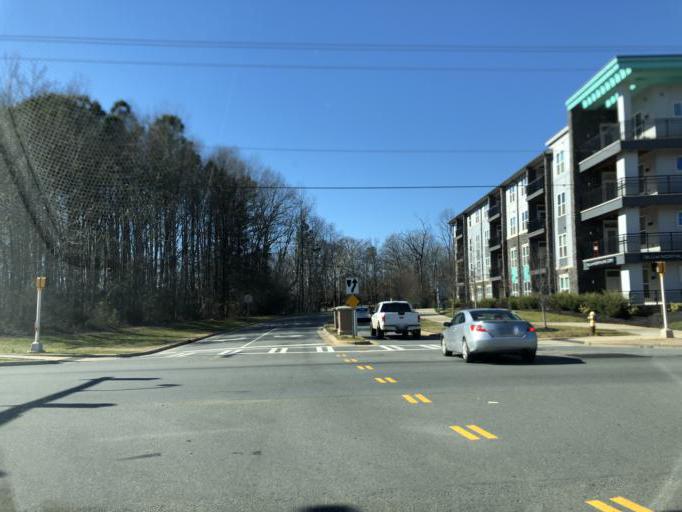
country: US
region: North Carolina
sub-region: Mecklenburg County
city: Charlotte
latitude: 35.2808
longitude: -80.7655
